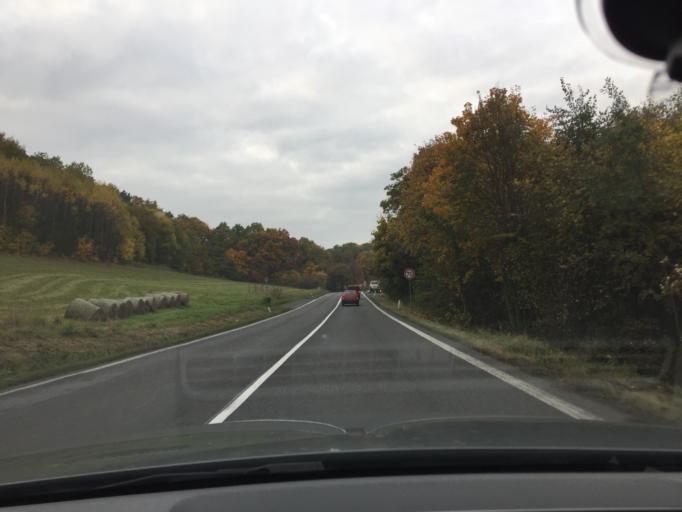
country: CZ
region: Ustecky
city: Rehlovice
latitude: 50.5710
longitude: 13.9432
